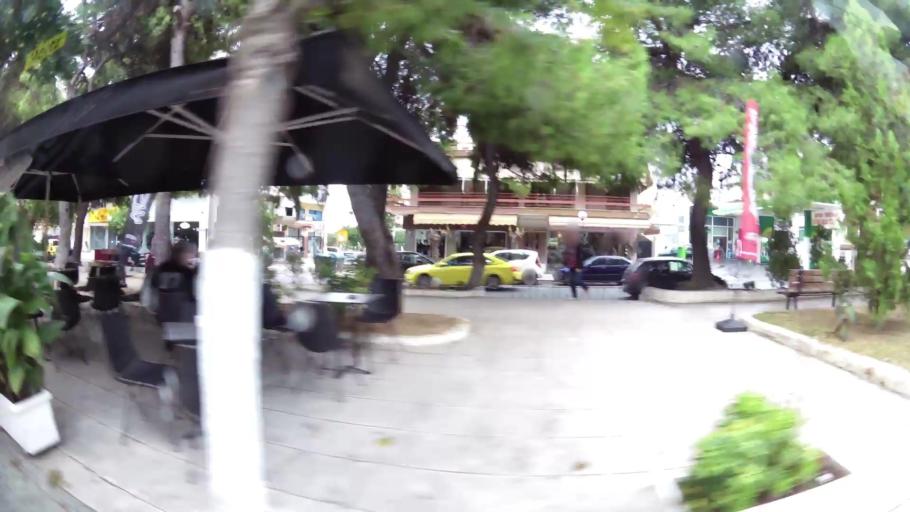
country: GR
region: Attica
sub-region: Nomarchia Athinas
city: Chaidari
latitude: 38.0080
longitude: 23.6649
